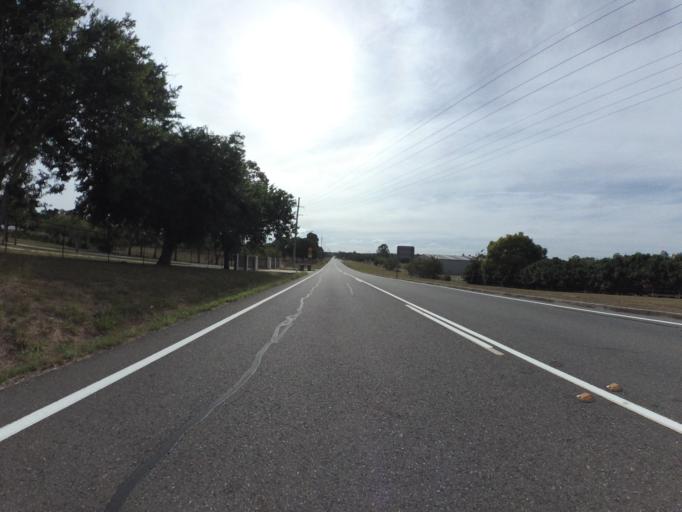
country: AU
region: Queensland
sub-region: Ipswich
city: Redbank
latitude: -27.5935
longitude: 152.8598
